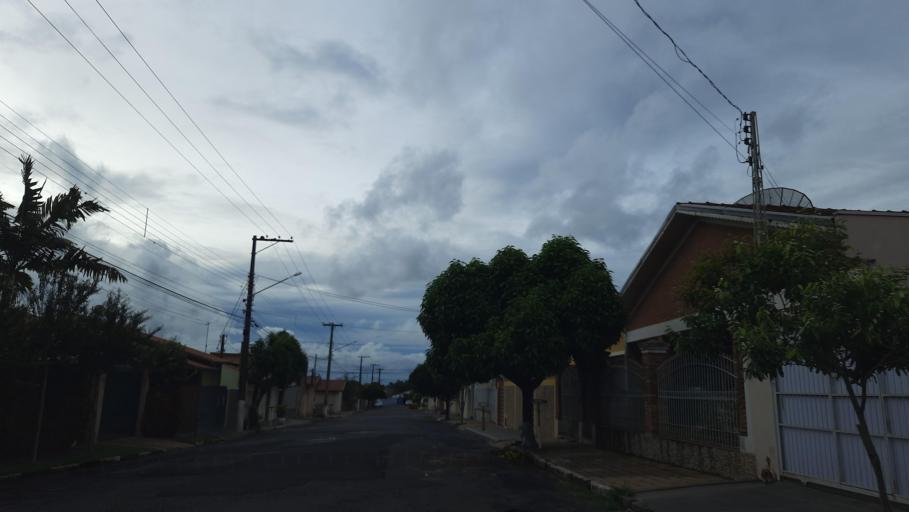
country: BR
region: Sao Paulo
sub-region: Casa Branca
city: Casa Branca
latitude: -21.7800
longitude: -47.0821
